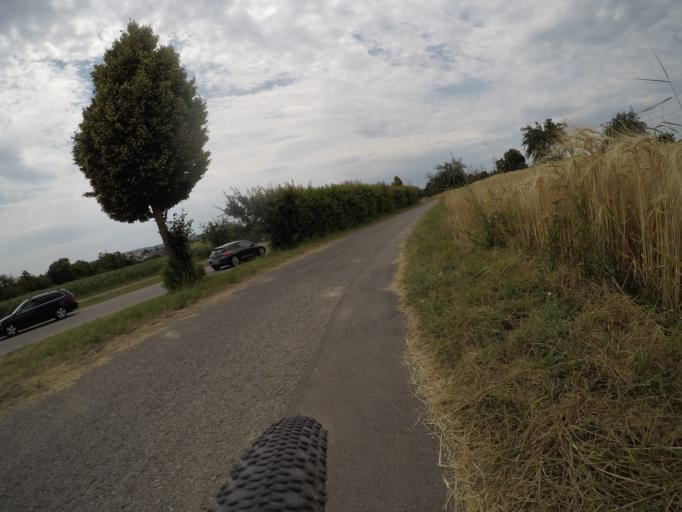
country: DE
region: Baden-Wuerttemberg
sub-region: Regierungsbezirk Stuttgart
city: Magstadt
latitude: 48.7220
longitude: 8.9565
